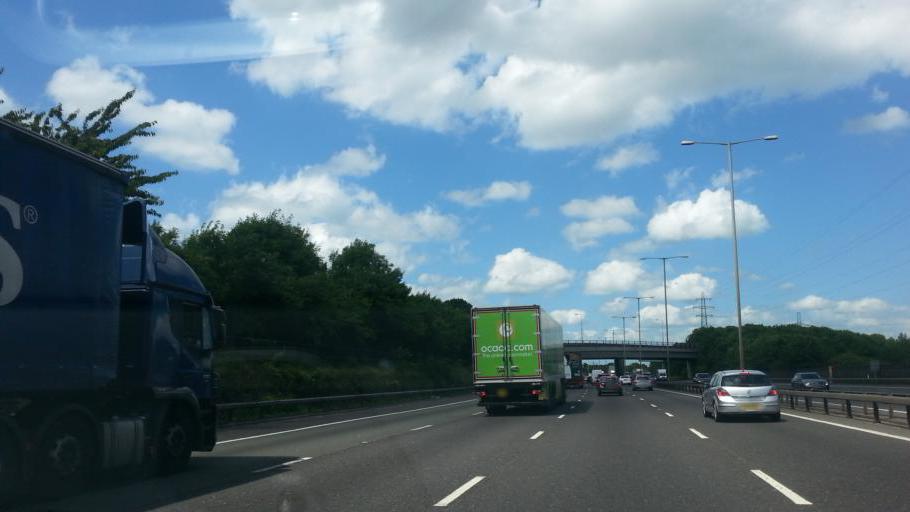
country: GB
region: England
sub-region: Buckinghamshire
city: Iver
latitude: 51.5201
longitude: -0.4987
